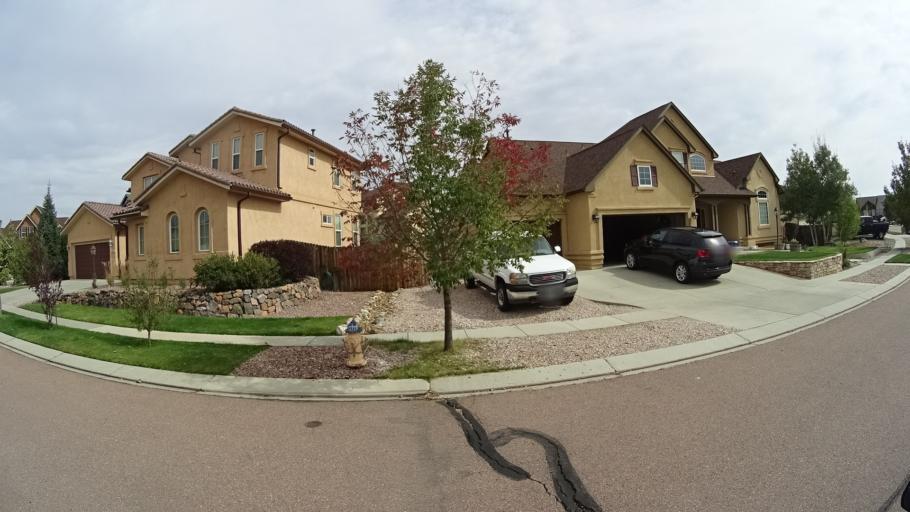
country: US
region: Colorado
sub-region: El Paso County
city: Cimarron Hills
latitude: 38.9227
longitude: -104.6950
